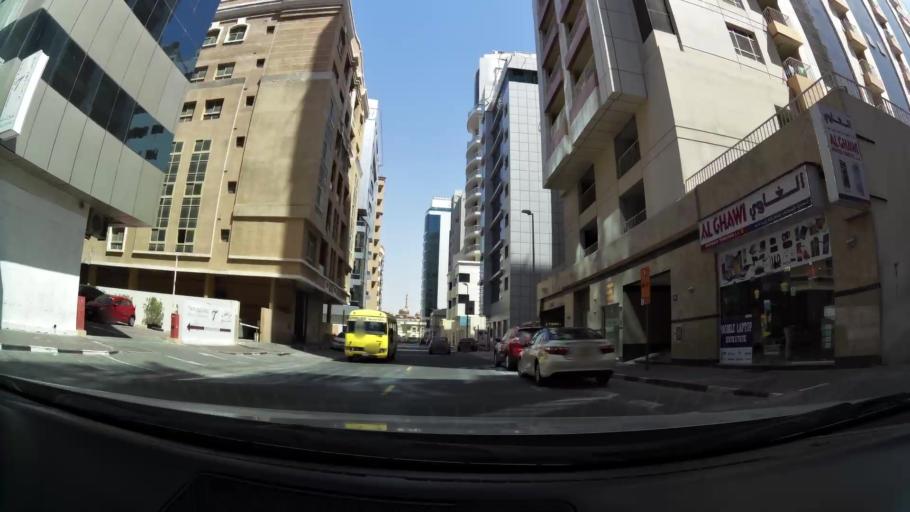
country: AE
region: Dubai
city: Dubai
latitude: 25.1102
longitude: 55.2030
